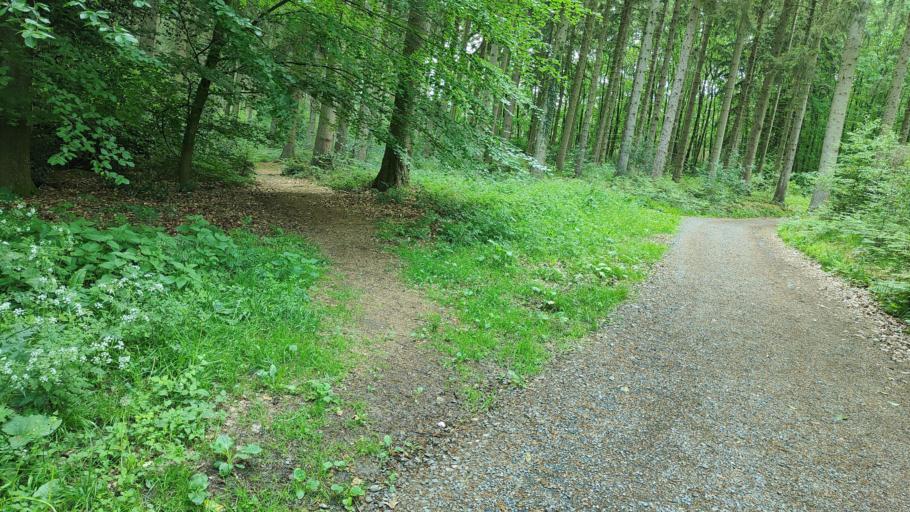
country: BE
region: Wallonia
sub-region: Province de Liege
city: La Calamine
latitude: 50.7160
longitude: 6.0597
